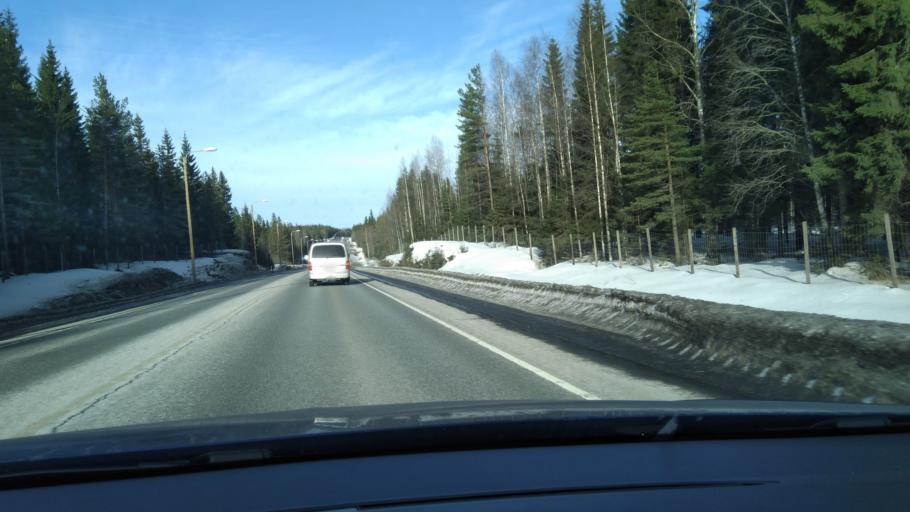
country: FI
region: Pirkanmaa
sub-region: Tampere
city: Orivesi
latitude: 61.6589
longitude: 24.2551
